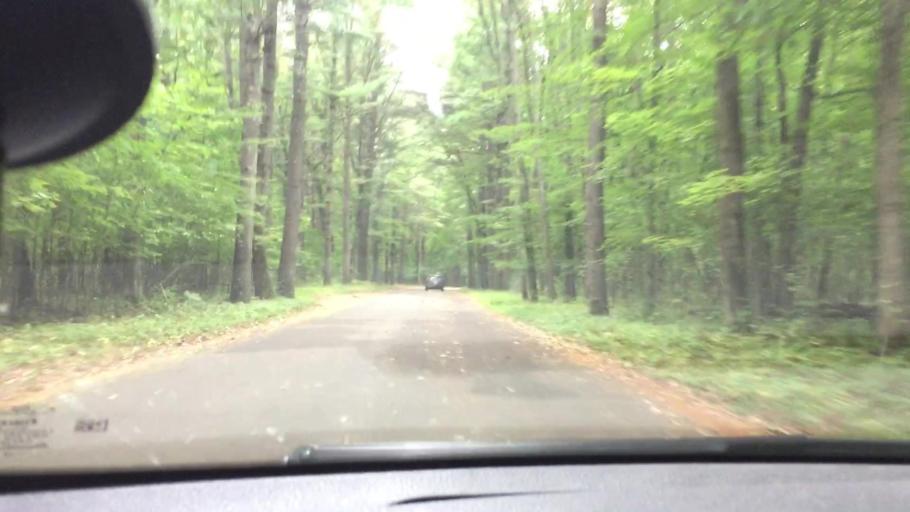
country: US
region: Wisconsin
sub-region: Chippewa County
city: Chippewa Falls
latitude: 44.9585
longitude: -91.4013
